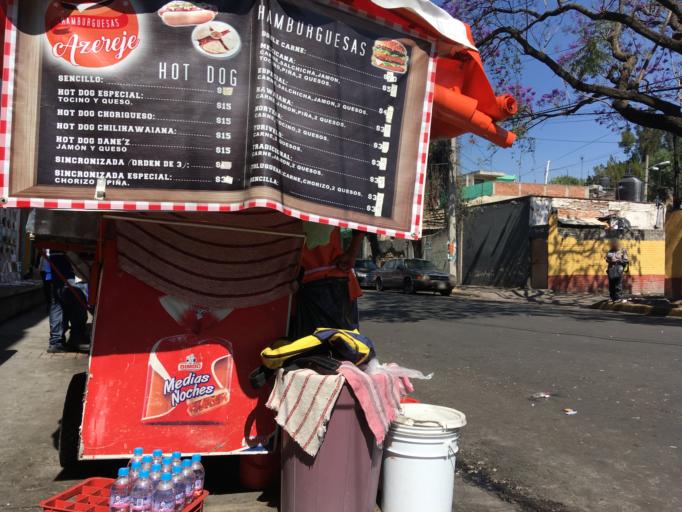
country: MX
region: Mexico City
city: Coyoacan
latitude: 19.3535
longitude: -99.1454
